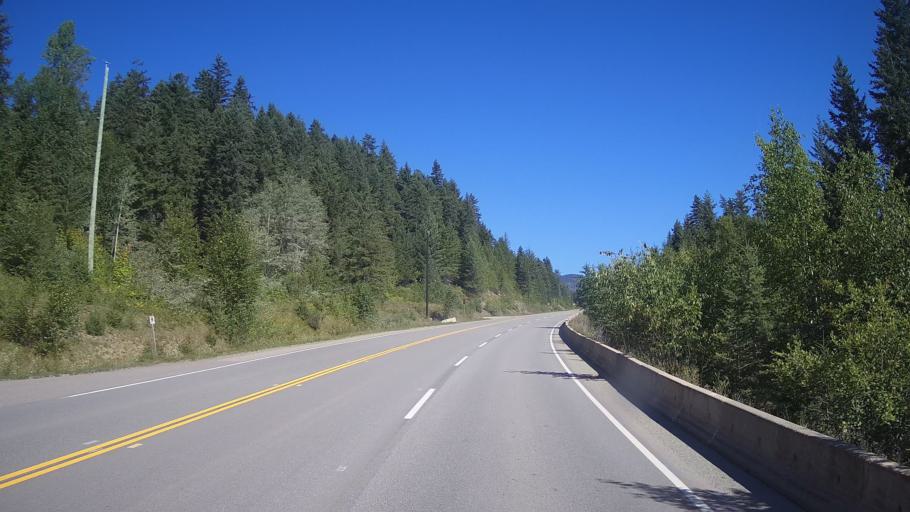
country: CA
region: British Columbia
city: Kamloops
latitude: 51.4576
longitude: -120.2283
